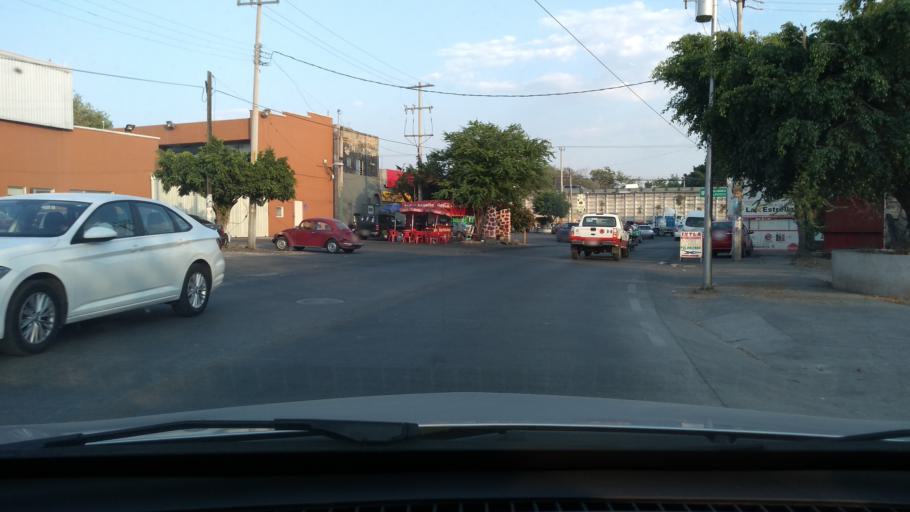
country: MX
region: Morelos
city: Puente de Ixtla
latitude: 18.6327
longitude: -99.3233
